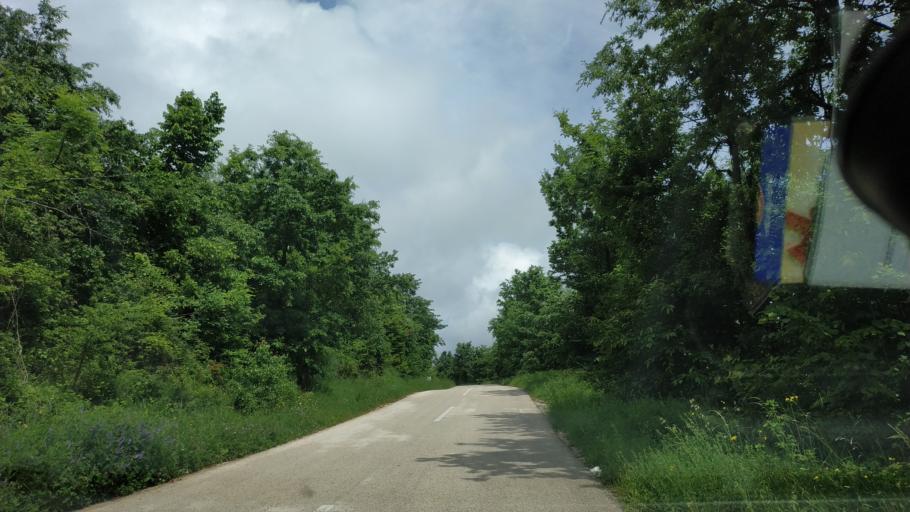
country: RS
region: Central Serbia
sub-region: Zajecarski Okrug
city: Boljevac
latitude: 43.7348
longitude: 21.9527
